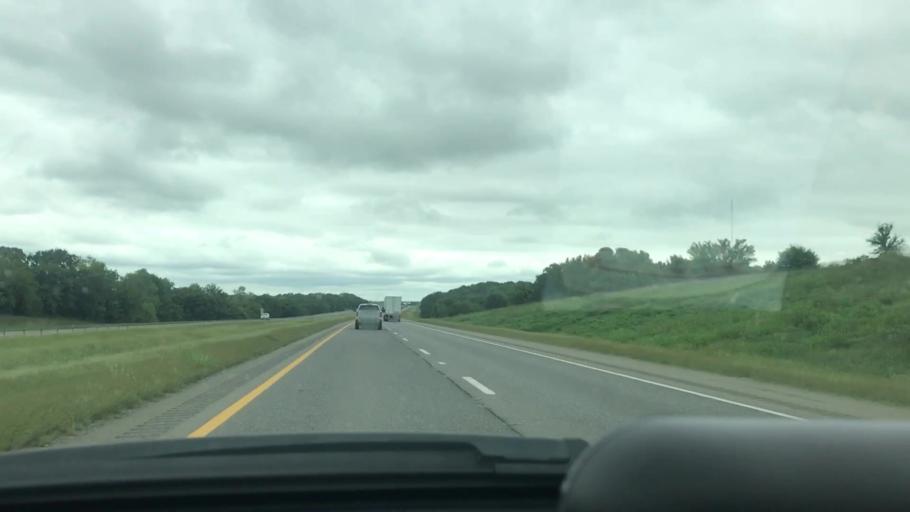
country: US
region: Oklahoma
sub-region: McIntosh County
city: Checotah
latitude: 35.3925
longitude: -95.5651
